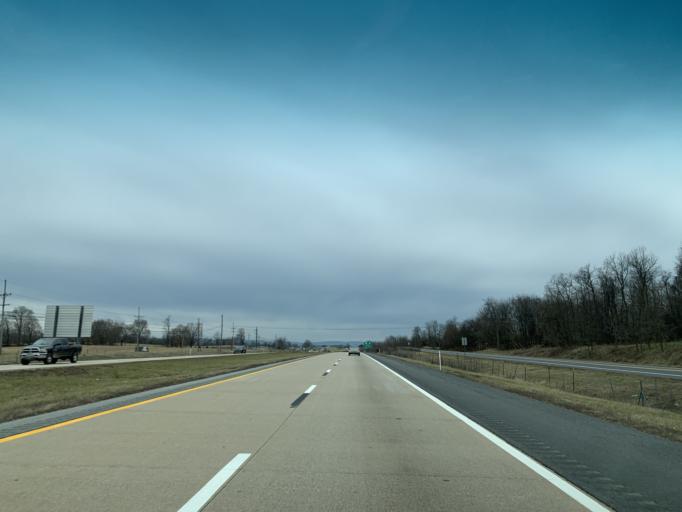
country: US
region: West Virginia
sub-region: Jefferson County
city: Ranson
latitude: 39.3471
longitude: -77.8558
